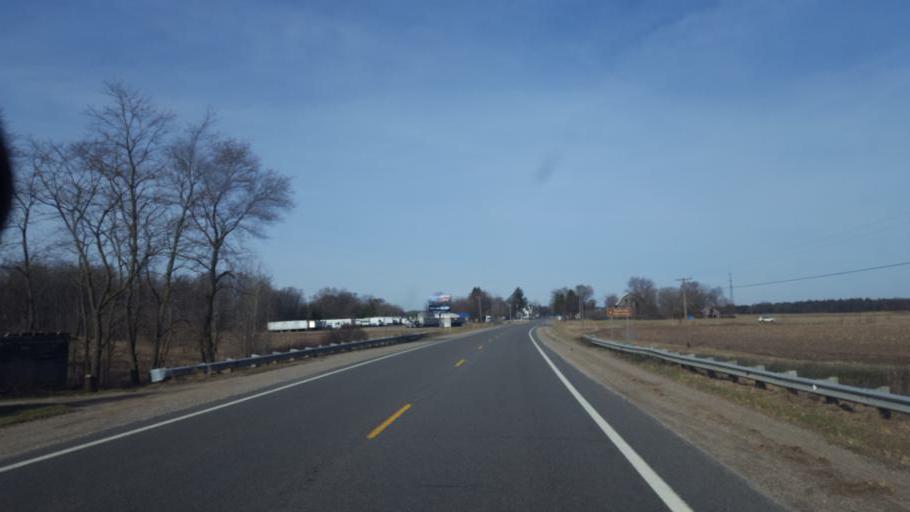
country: US
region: Michigan
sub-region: Montcalm County
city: Howard City
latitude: 43.4317
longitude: -85.3803
